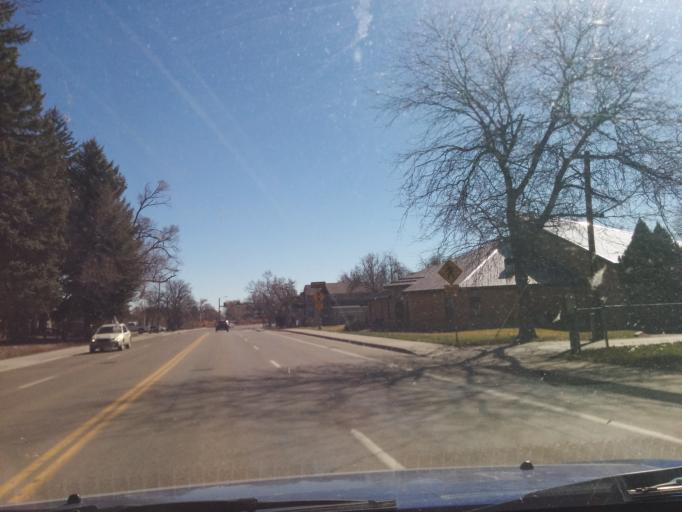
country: US
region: Colorado
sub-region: Larimer County
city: Fort Collins
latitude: 40.5819
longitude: -105.1086
